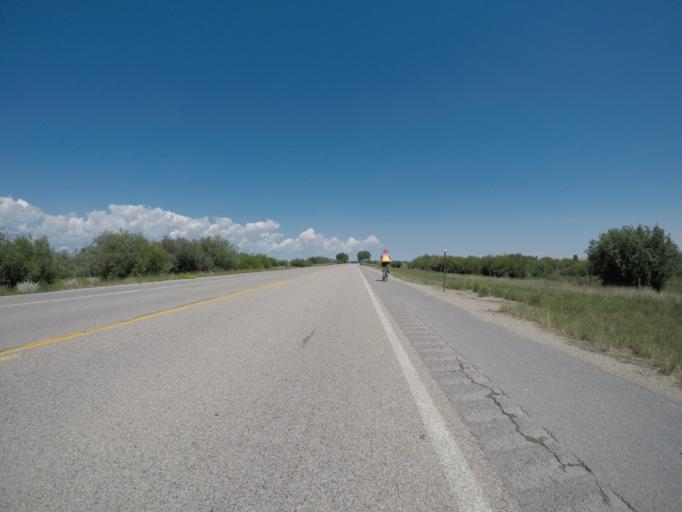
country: US
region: Wyoming
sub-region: Sublette County
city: Marbleton
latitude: 42.5215
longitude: -110.1069
